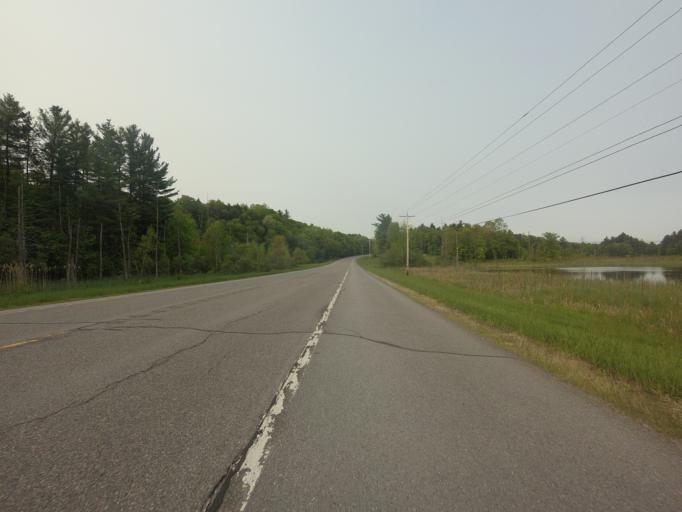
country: US
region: New York
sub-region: Jefferson County
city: Carthage
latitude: 44.0979
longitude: -75.4157
